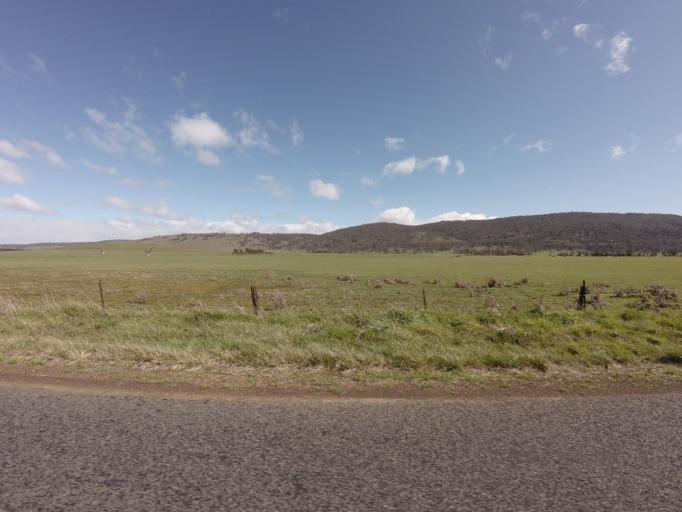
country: AU
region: Tasmania
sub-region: Northern Midlands
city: Evandale
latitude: -41.9875
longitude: 147.4513
